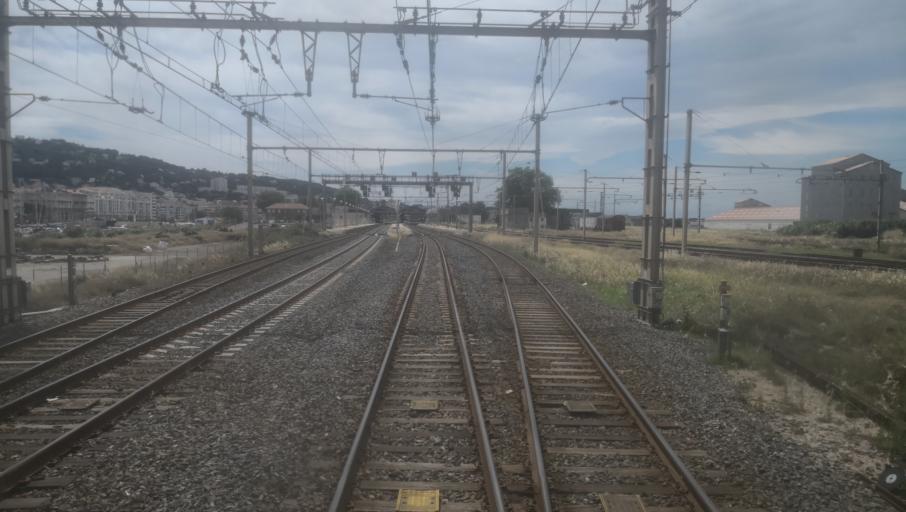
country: FR
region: Languedoc-Roussillon
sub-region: Departement de l'Herault
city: Sete
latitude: 43.4133
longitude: 3.6988
